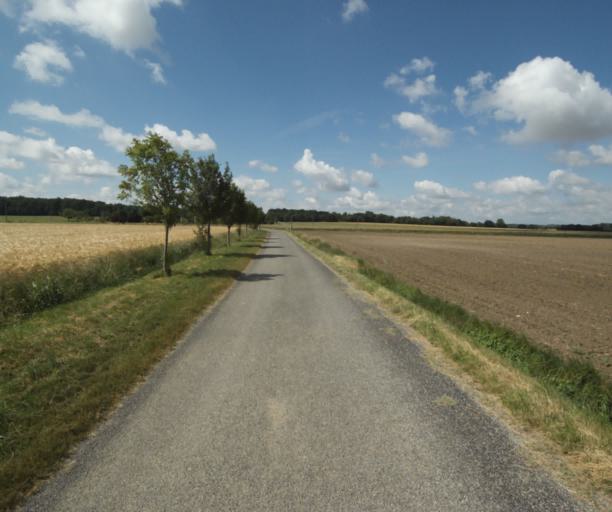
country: FR
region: Midi-Pyrenees
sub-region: Departement de la Haute-Garonne
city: Saint-Felix-Lauragais
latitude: 43.4362
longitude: 1.9223
